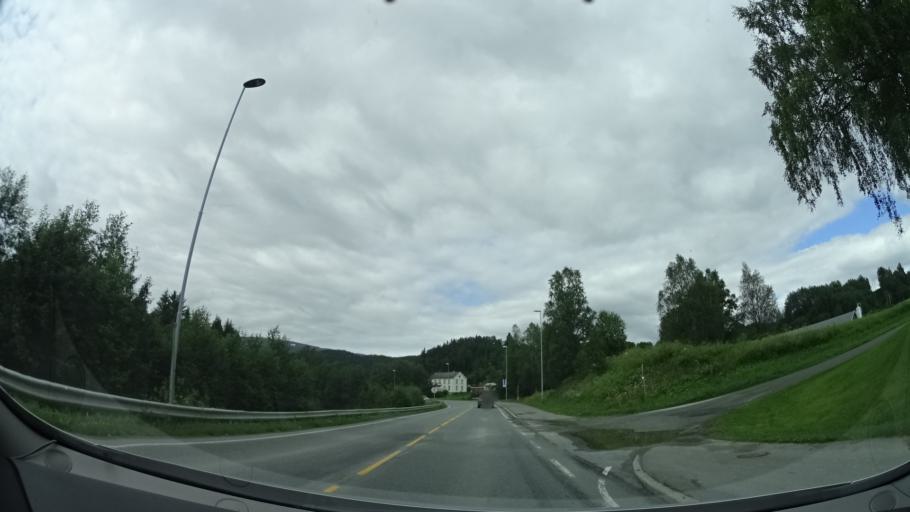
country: NO
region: Nord-Trondelag
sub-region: Meraker
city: Meraker
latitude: 63.4227
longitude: 11.7342
